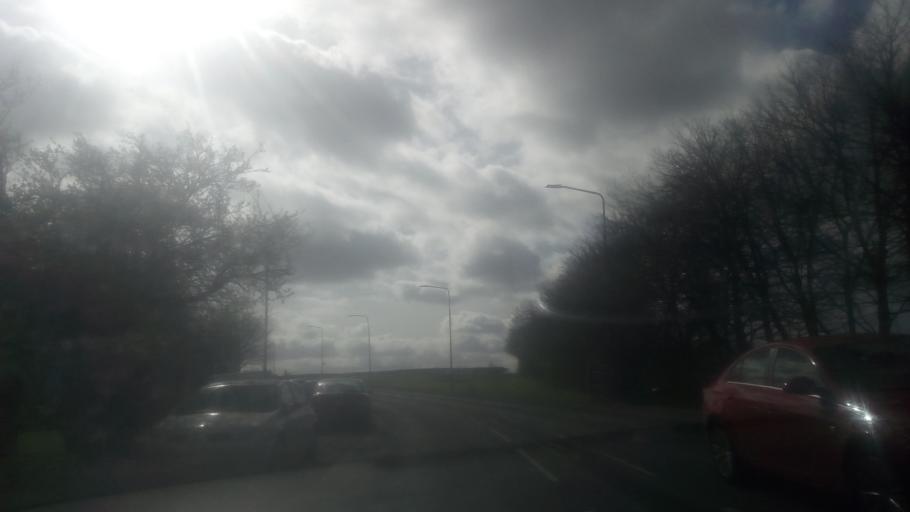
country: GB
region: Scotland
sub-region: East Lothian
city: Tranent
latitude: 55.9419
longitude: -2.9625
